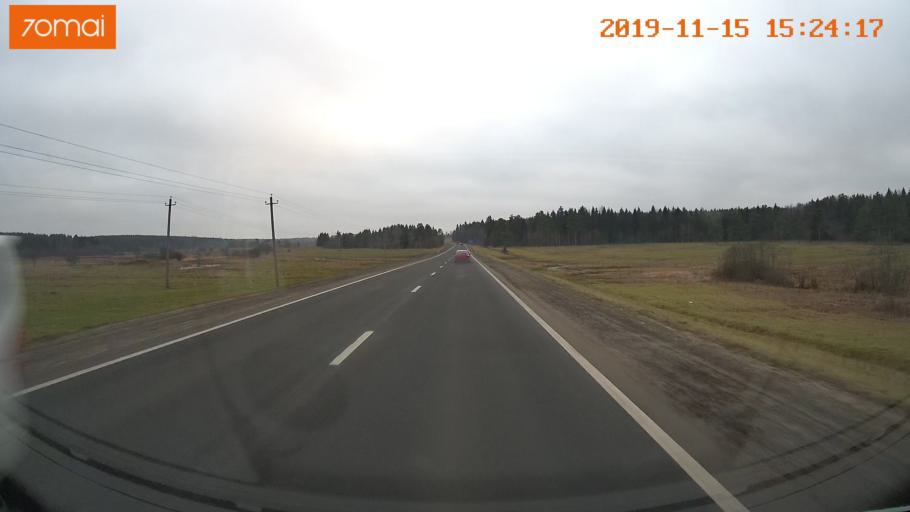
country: RU
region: Jaroslavl
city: Danilov
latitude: 58.1797
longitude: 40.1328
